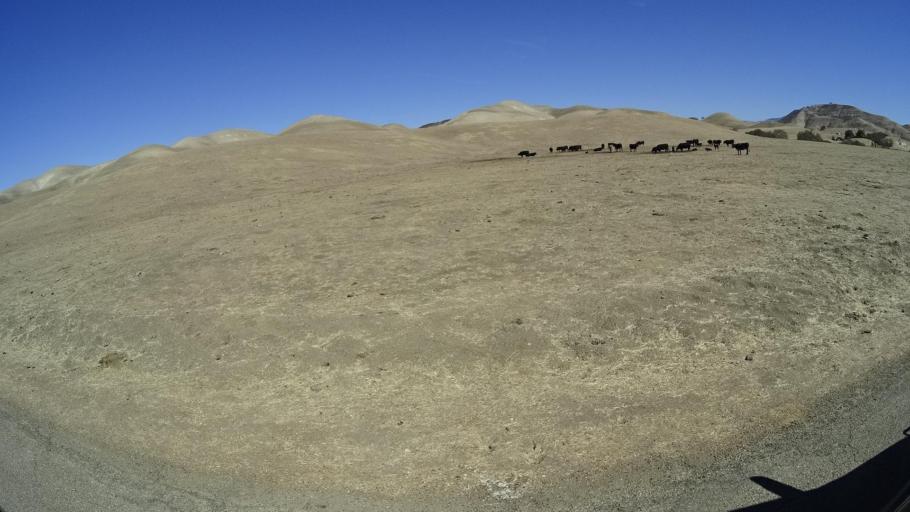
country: US
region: California
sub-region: San Luis Obispo County
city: San Miguel
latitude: 36.0617
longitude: -120.7930
